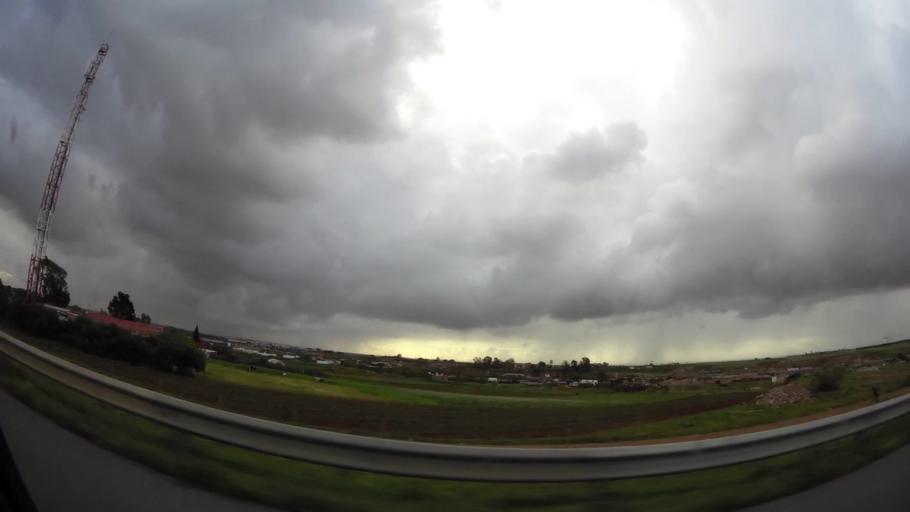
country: MA
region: Grand Casablanca
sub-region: Mediouna
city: Tit Mellil
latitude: 33.6030
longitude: -7.4372
